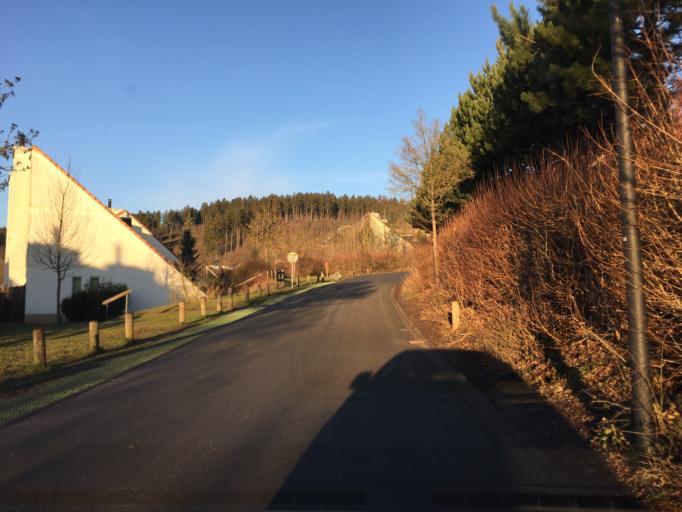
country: DE
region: North Rhine-Westphalia
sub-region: Regierungsbezirk Arnsberg
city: Medebach
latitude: 51.2092
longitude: 8.6874
